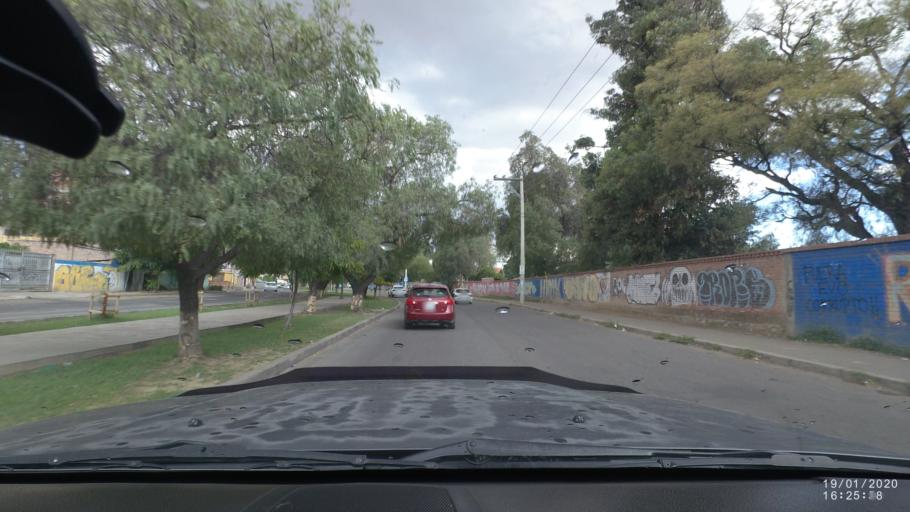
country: BO
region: Cochabamba
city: Cochabamba
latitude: -17.3881
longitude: -66.1816
